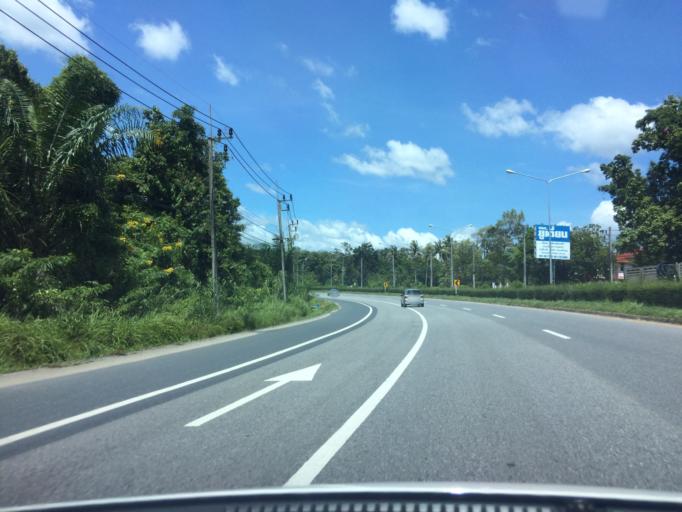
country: TH
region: Phangnga
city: Thai Mueang
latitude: 8.2271
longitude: 98.3000
